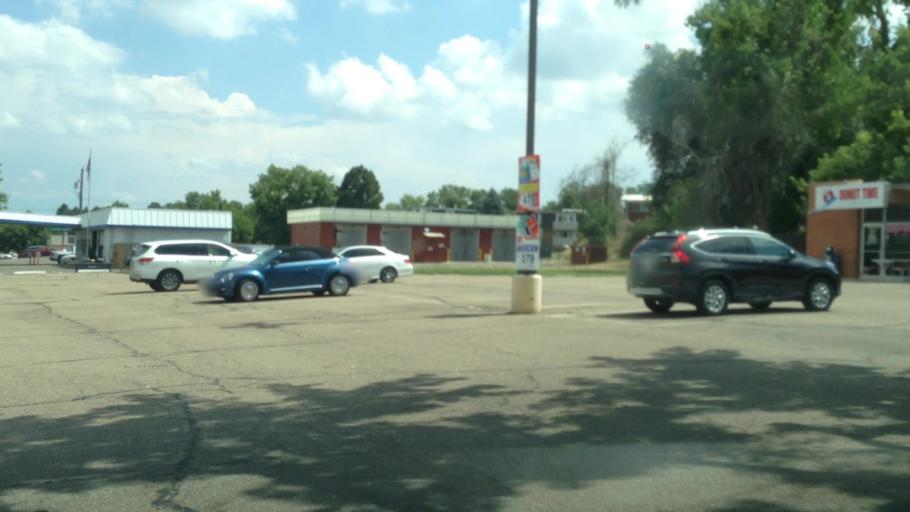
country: US
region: Colorado
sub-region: Jefferson County
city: Arvada
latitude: 39.8114
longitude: -105.1138
